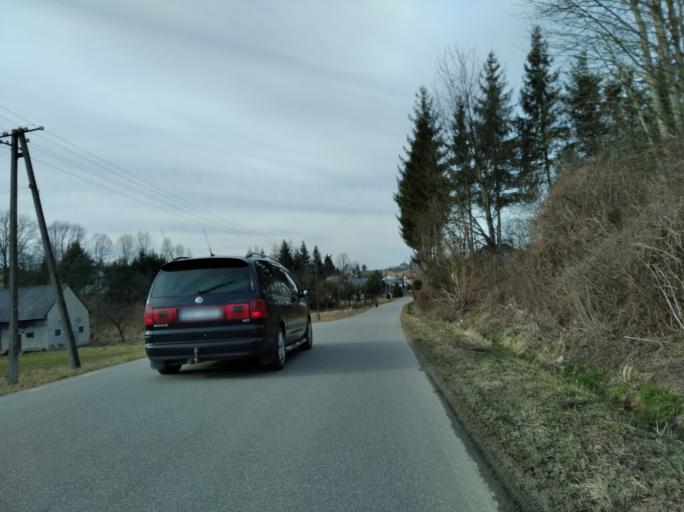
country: PL
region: Subcarpathian Voivodeship
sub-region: Powiat brzozowski
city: Gorki
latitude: 49.6409
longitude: 22.0537
